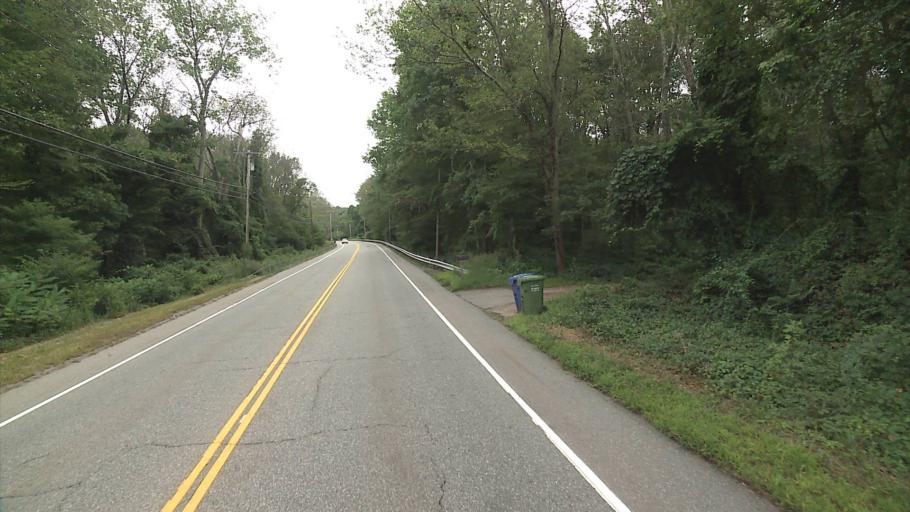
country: US
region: Connecticut
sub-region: Hartford County
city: Terramuggus
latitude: 41.6892
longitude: -72.4298
